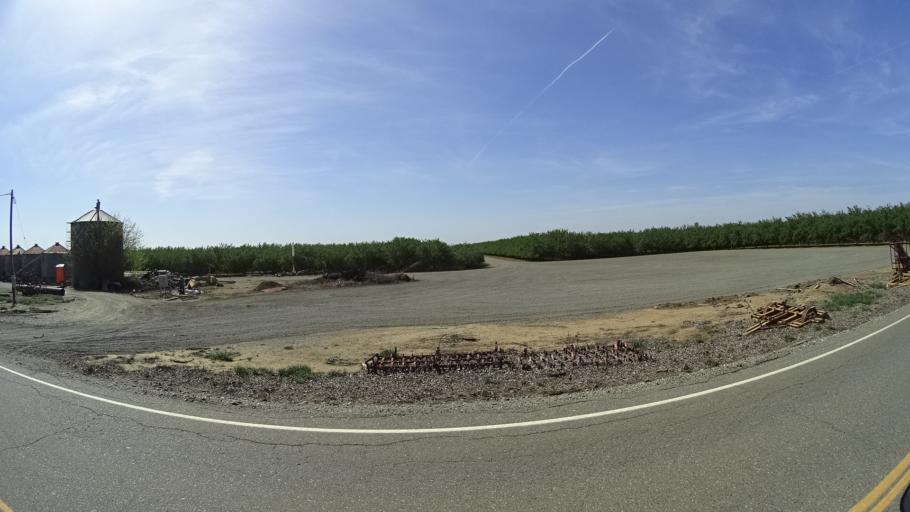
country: US
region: California
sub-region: Glenn County
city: Willows
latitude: 39.5389
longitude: -122.2525
